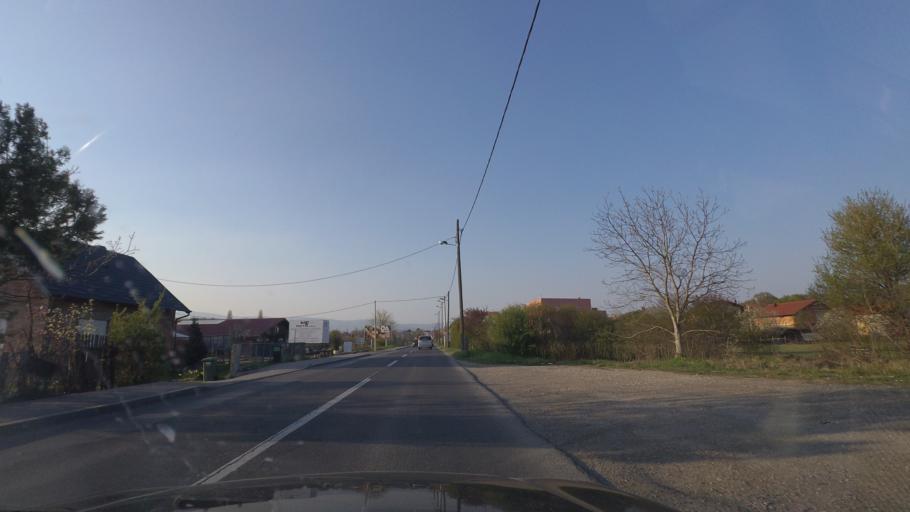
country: HR
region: Grad Zagreb
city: Dubrava
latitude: 45.8130
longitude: 16.0664
